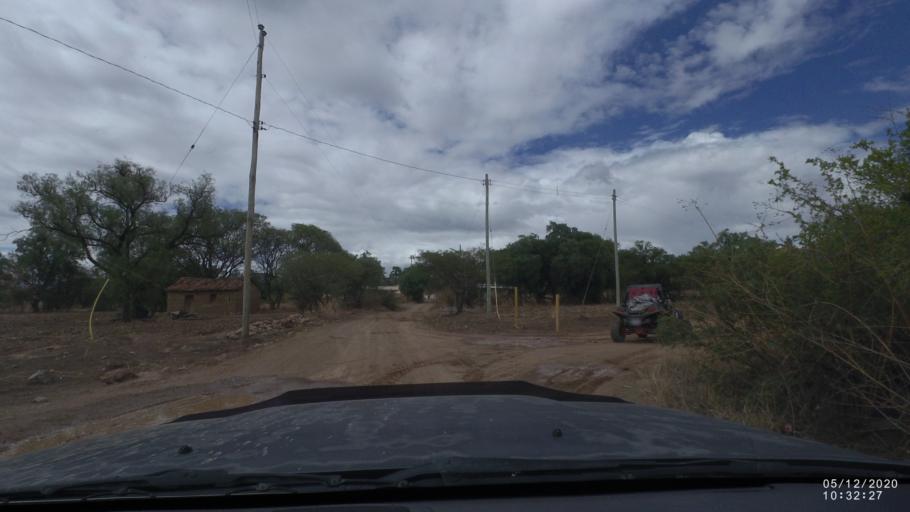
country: BO
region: Cochabamba
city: Sipe Sipe
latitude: -17.5458
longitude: -66.2695
